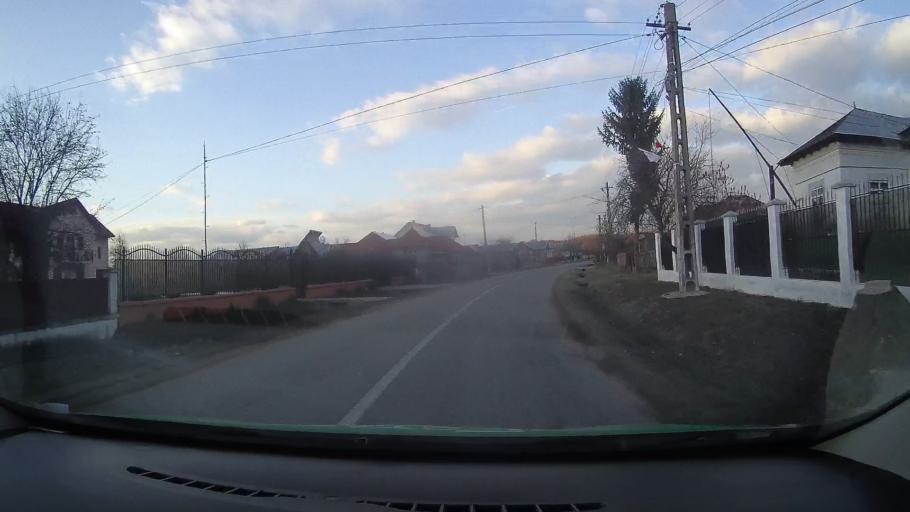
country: RO
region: Dambovita
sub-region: Comuna Gura Ocnitei
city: Adanca
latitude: 44.9128
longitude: 25.6148
